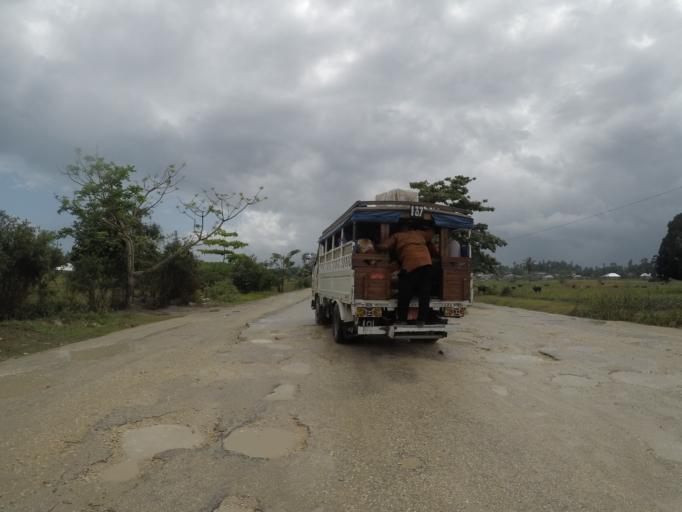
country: TZ
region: Zanzibar Central/South
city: Koani
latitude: -6.0787
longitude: 39.2222
